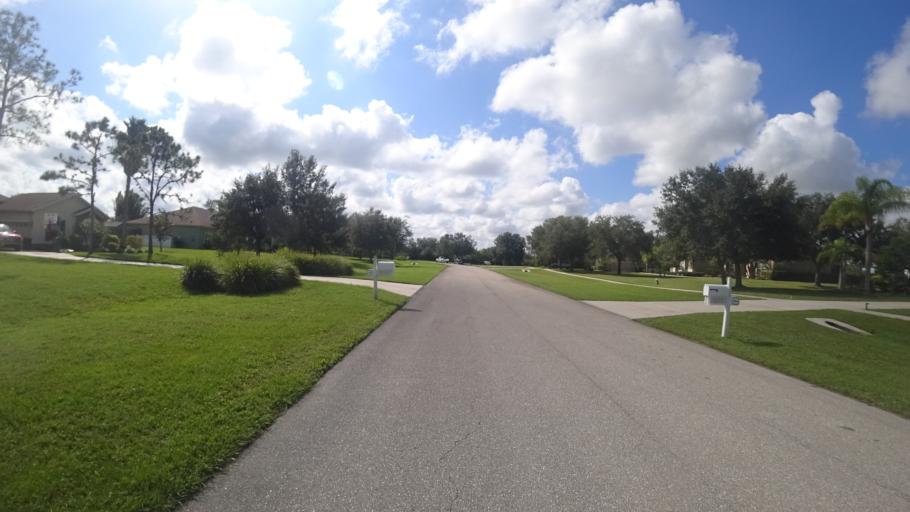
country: US
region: Florida
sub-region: Sarasota County
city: Fruitville
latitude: 27.3974
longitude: -82.3067
